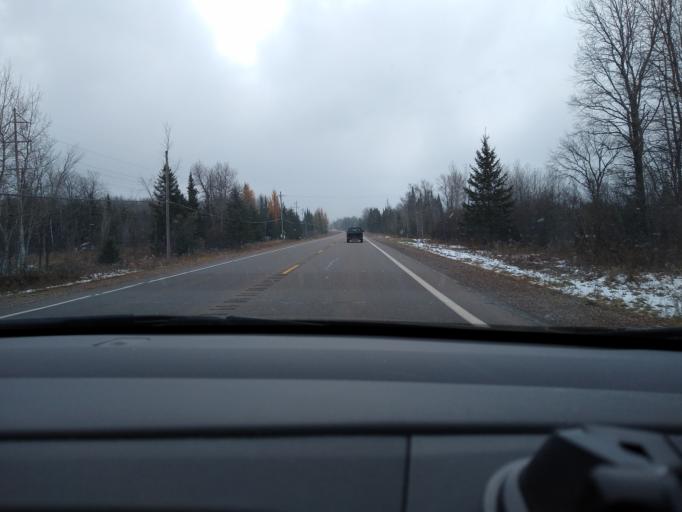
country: US
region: Michigan
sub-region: Dickinson County
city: Iron Mountain
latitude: 46.0293
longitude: -88.0601
